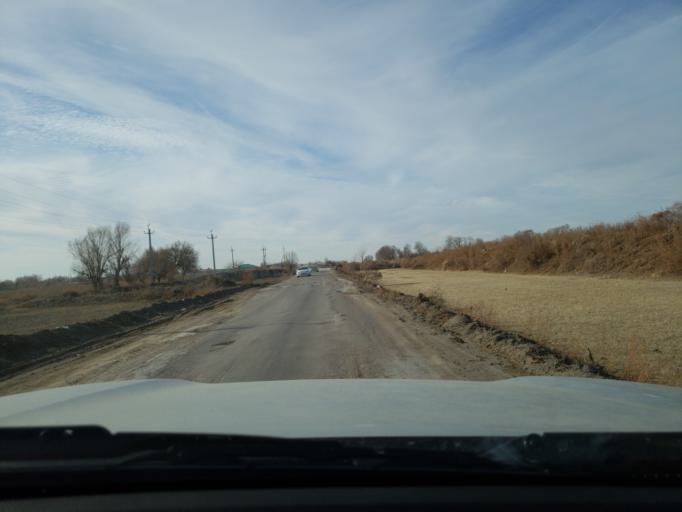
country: TM
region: Dasoguz
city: Dasoguz
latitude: 41.8492
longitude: 59.8841
